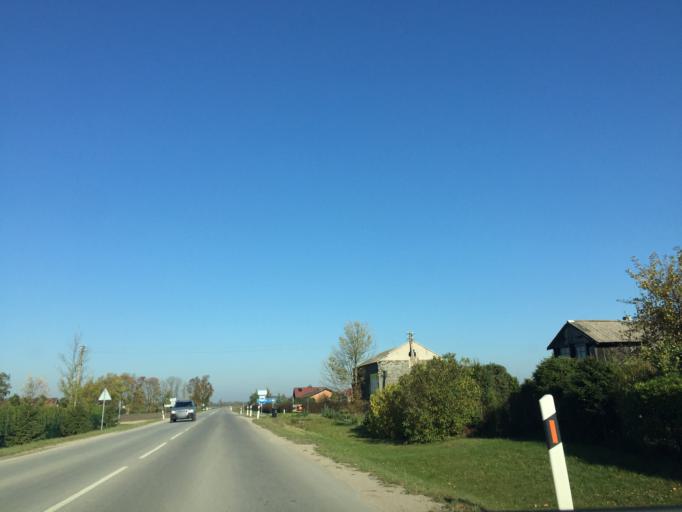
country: LT
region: Klaipedos apskritis
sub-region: Klaipeda
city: Klaipeda
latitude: 55.7633
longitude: 21.1963
